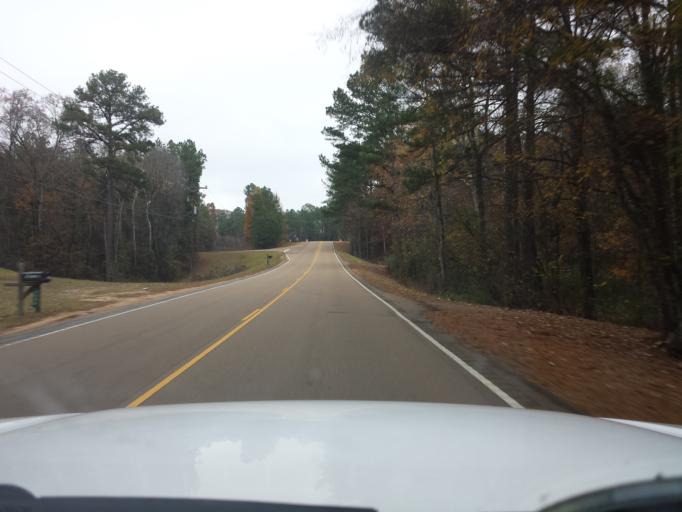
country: US
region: Mississippi
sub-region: Madison County
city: Canton
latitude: 32.4684
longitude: -89.9143
